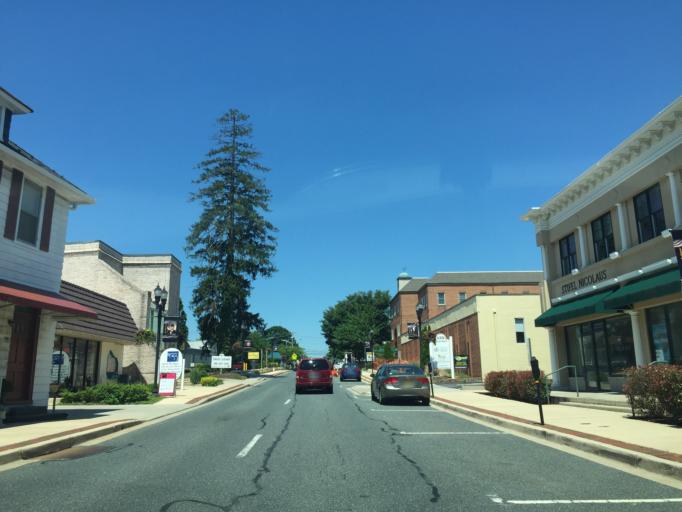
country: US
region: Maryland
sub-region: Harford County
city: Bel Air
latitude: 39.5378
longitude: -76.3511
